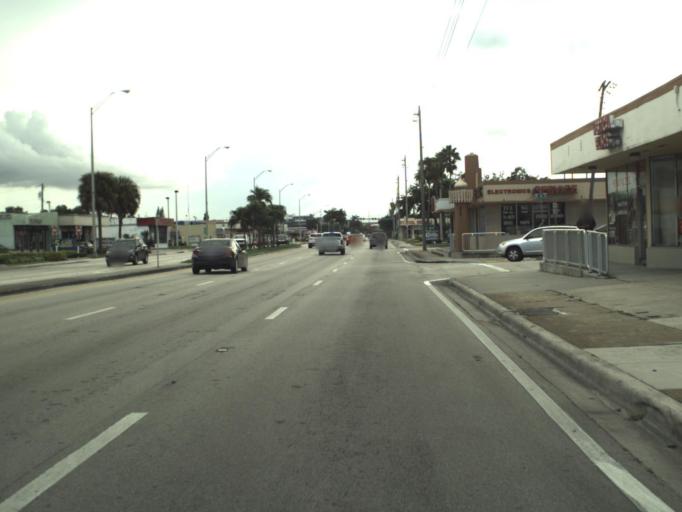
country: US
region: Florida
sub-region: Miami-Dade County
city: Golden Glades
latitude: 25.9286
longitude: -80.1904
